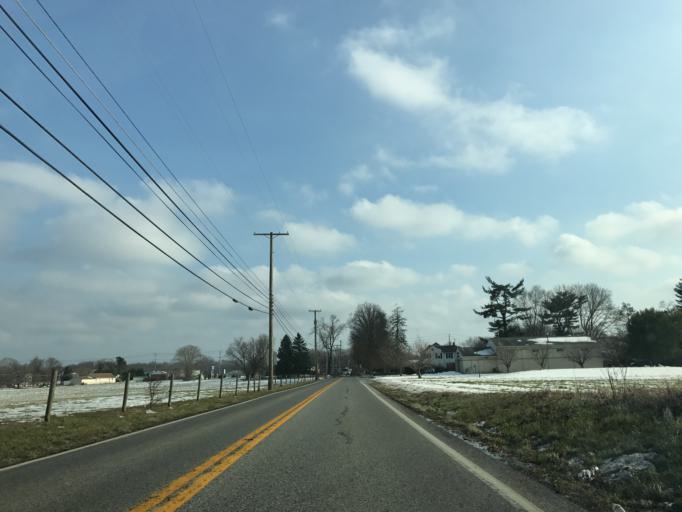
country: US
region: Maryland
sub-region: Harford County
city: Bel Air South
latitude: 39.5623
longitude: -76.2529
